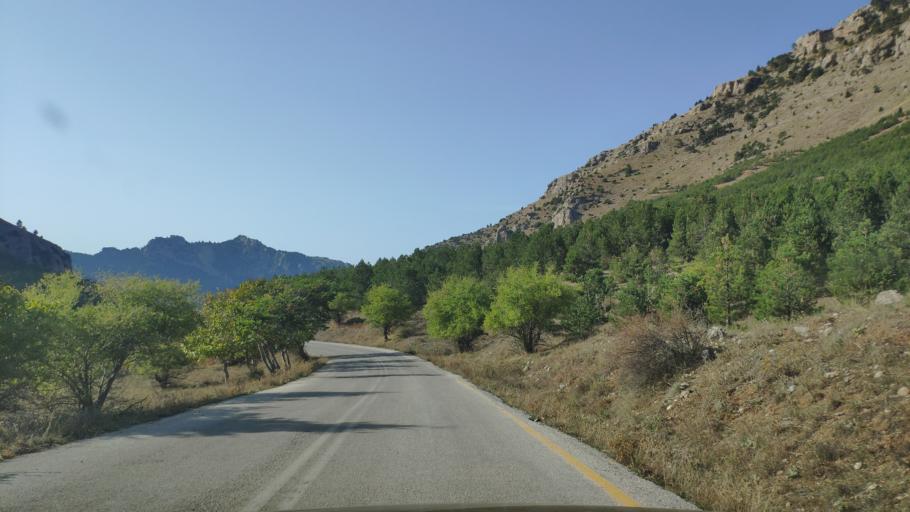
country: GR
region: West Greece
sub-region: Nomos Achaias
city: Aiyira
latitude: 38.0394
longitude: 22.3965
